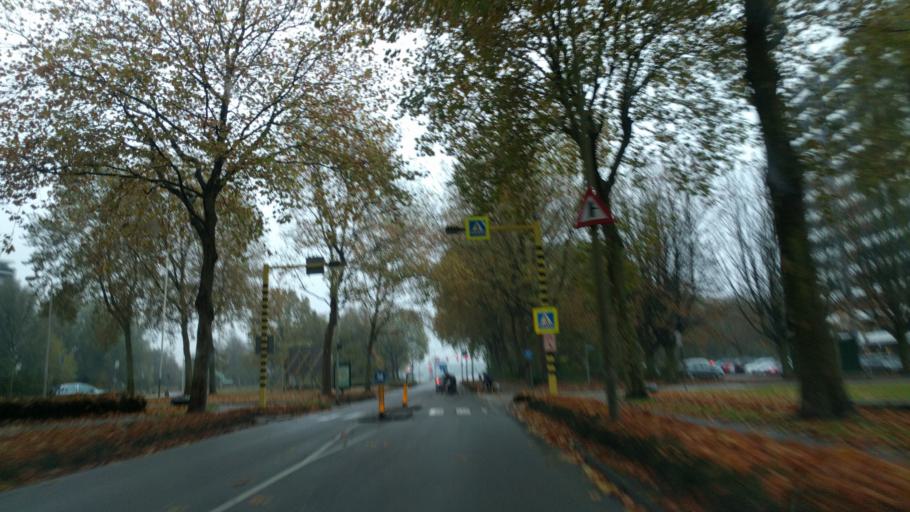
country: NL
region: South Holland
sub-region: Gemeente Ridderkerk
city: Ridderkerk
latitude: 51.8886
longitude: 4.5818
